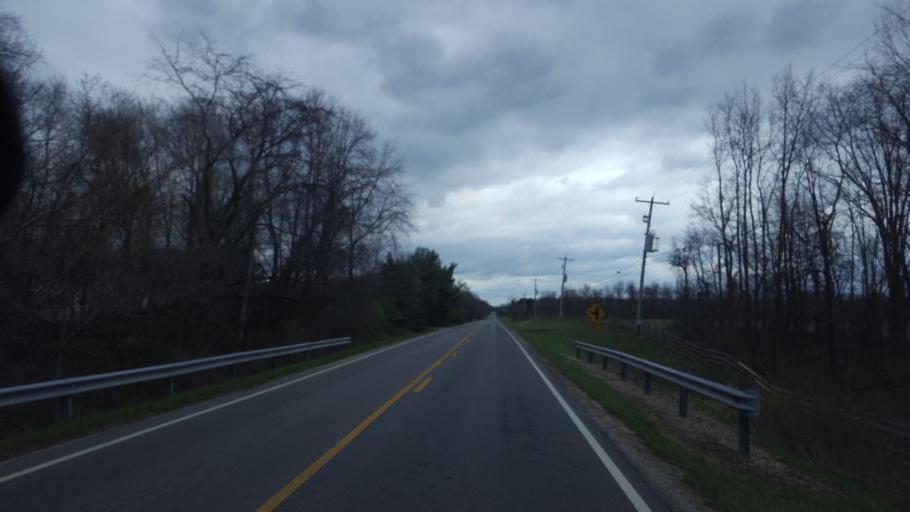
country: US
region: Ohio
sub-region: Delaware County
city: Sunbury
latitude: 40.1958
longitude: -82.8715
